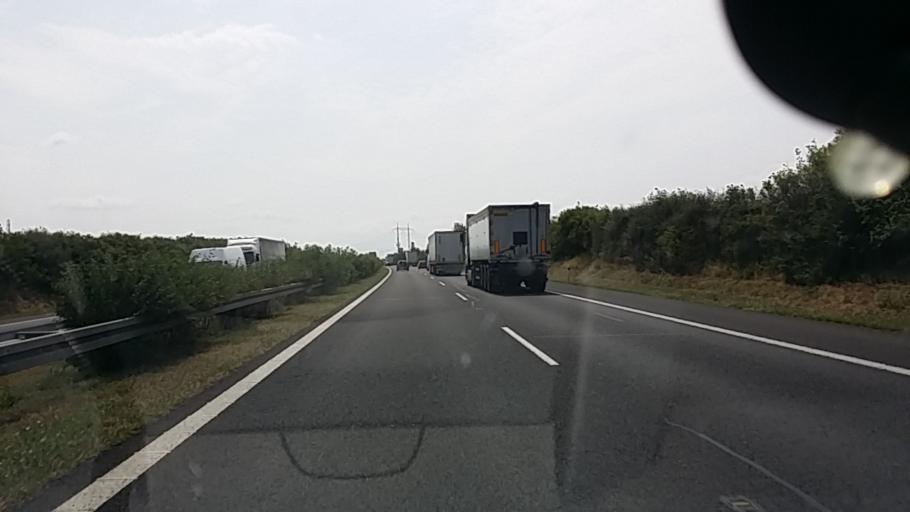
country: CZ
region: Ustecky
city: Lovosice
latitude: 50.4863
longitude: 14.0778
